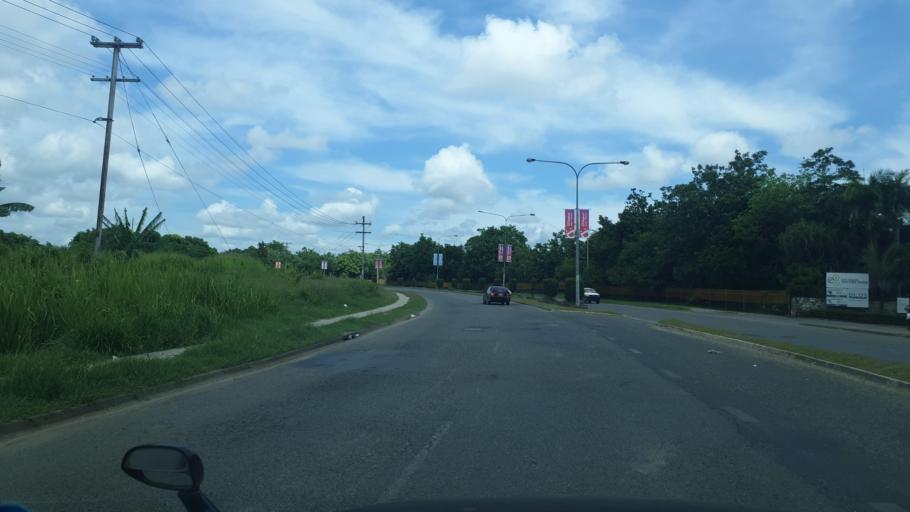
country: PG
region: National Capital
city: Port Moresby
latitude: -9.4058
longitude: 147.1646
